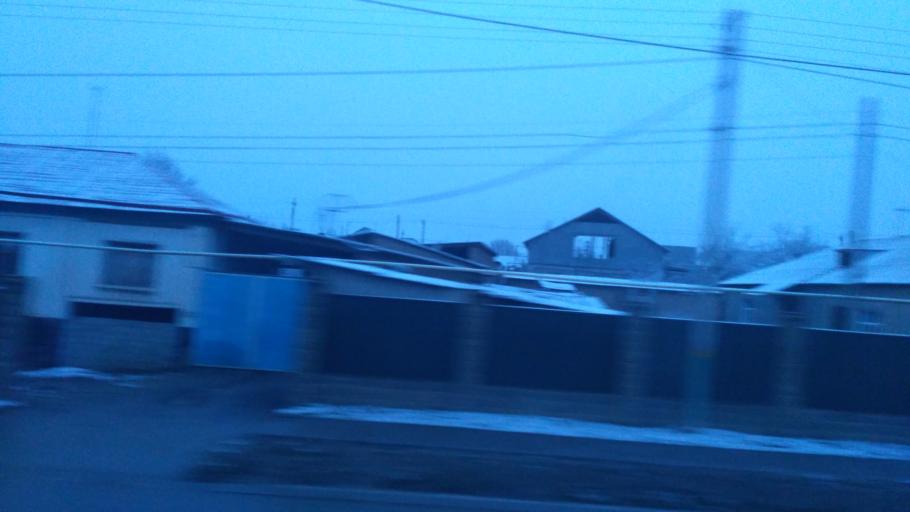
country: KZ
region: Ongtustik Qazaqstan
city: Shymkent
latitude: 42.3693
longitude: 69.5088
